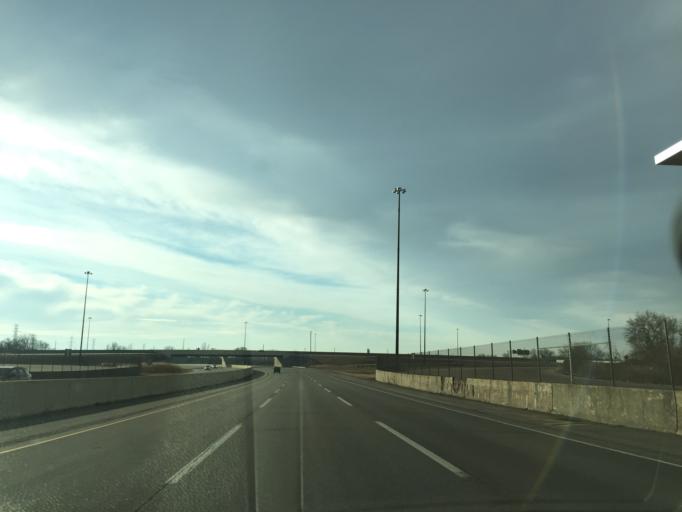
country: US
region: Indiana
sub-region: Lake County
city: Gary
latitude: 41.5923
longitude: -87.3051
